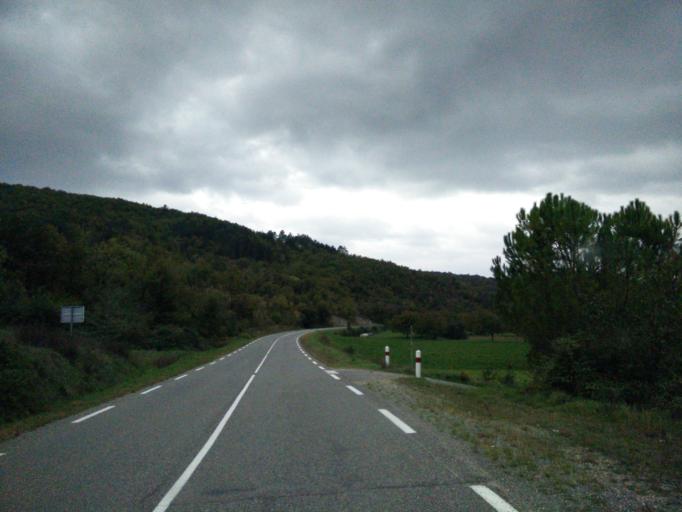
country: FR
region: Midi-Pyrenees
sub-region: Departement du Lot
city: Luzech
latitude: 44.5165
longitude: 1.2726
